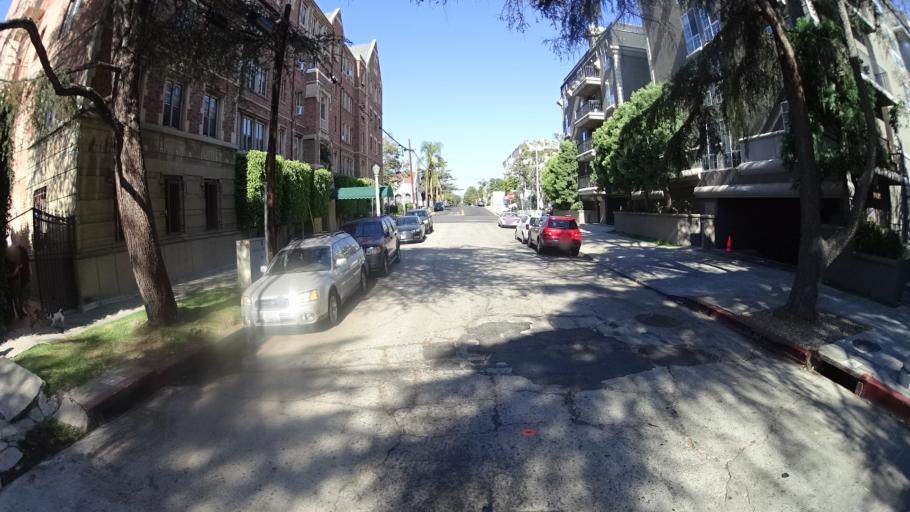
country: US
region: California
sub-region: Los Angeles County
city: Hollywood
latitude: 34.0817
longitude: -118.3278
